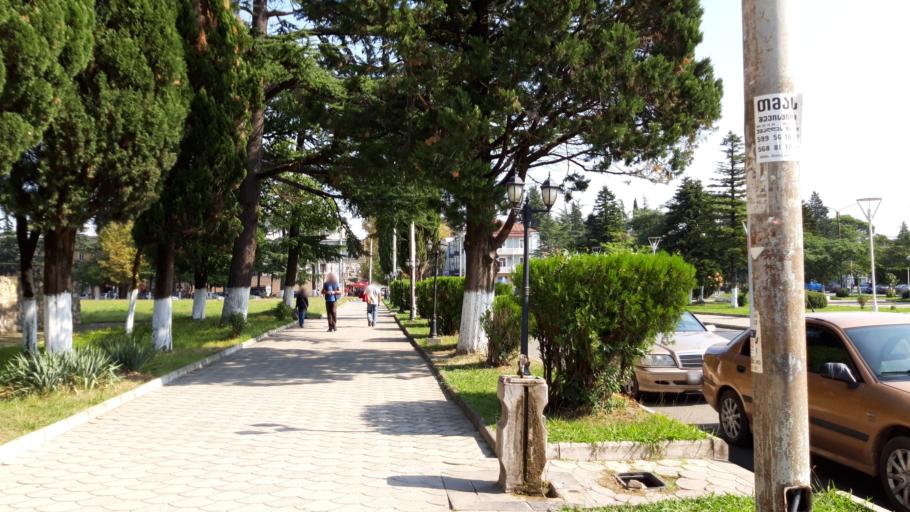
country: GE
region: Imereti
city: Samtredia
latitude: 42.1627
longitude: 42.3455
